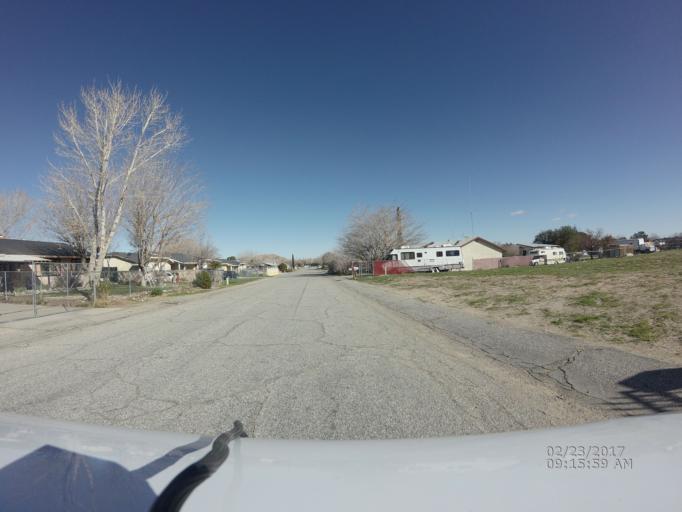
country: US
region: California
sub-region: Los Angeles County
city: Lake Los Angeles
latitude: 34.6134
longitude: -117.8420
